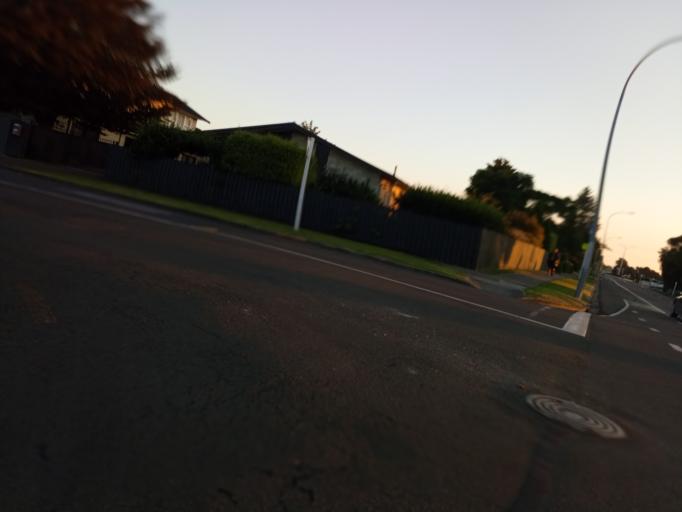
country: NZ
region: Gisborne
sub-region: Gisborne District
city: Gisborne
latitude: -38.6413
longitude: 178.0031
